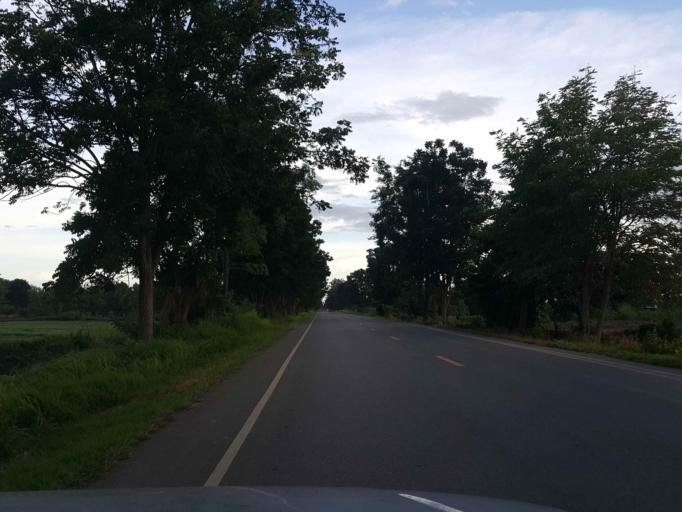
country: TH
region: Sukhothai
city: Sawankhalok
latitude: 17.3611
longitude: 99.7419
